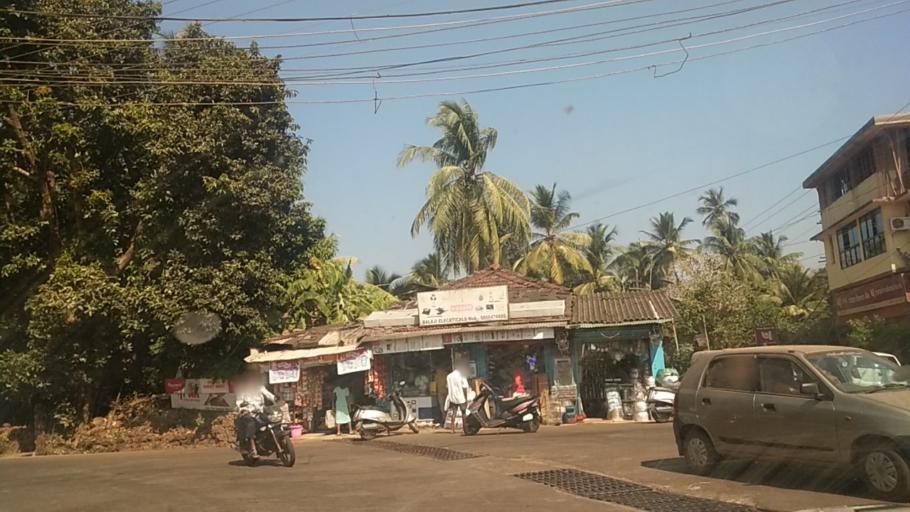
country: IN
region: Goa
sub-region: South Goa
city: Raia
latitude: 15.3203
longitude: 74.0298
